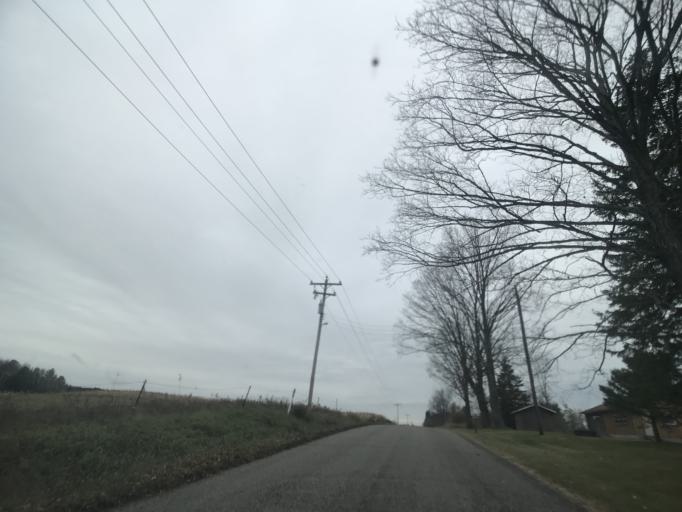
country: US
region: Wisconsin
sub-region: Menominee County
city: Legend Lake
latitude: 45.1812
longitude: -88.4596
